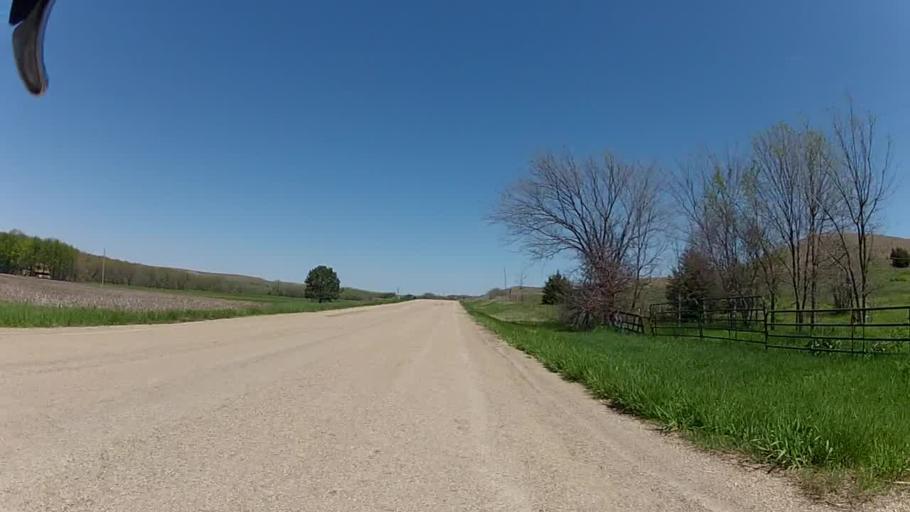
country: US
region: Kansas
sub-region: Riley County
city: Ogden
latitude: 38.9818
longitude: -96.5894
